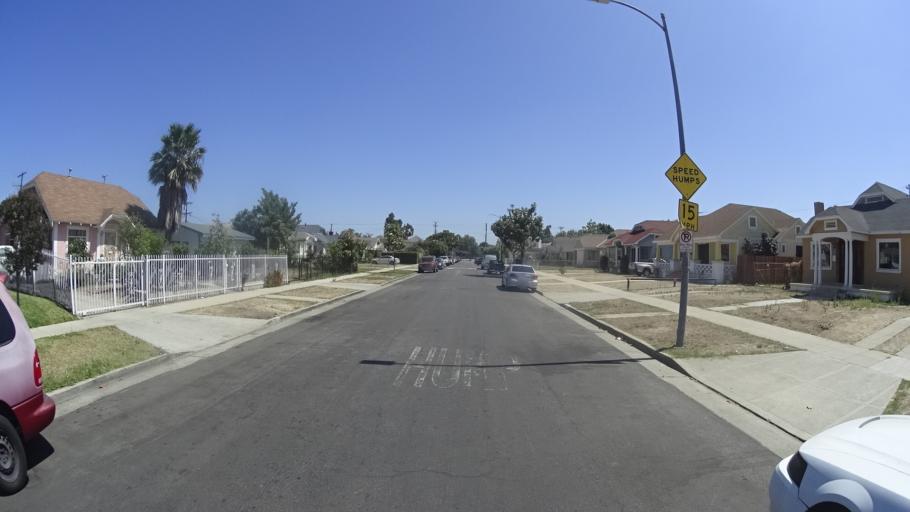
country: US
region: California
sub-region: Los Angeles County
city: View Park-Windsor Hills
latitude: 34.0052
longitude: -118.2988
